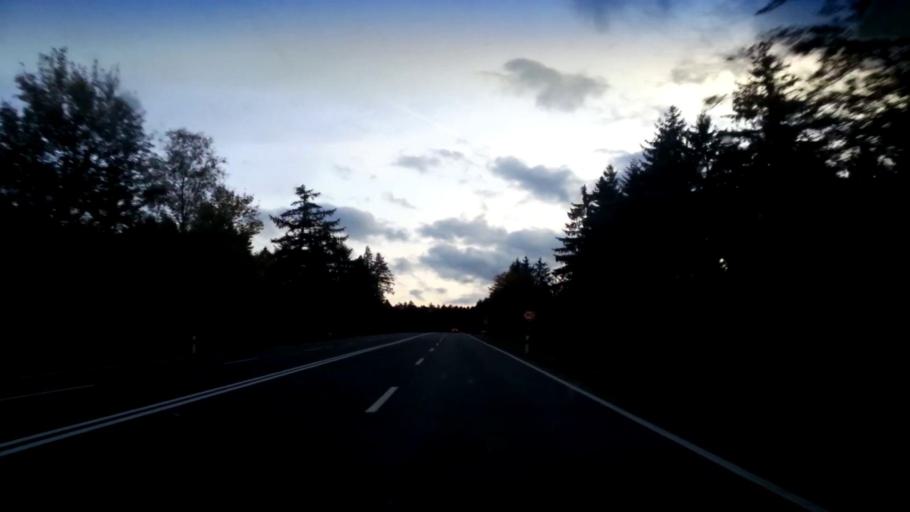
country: DE
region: Bavaria
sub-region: Upper Franconia
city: Nagel
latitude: 50.0067
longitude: 11.9234
